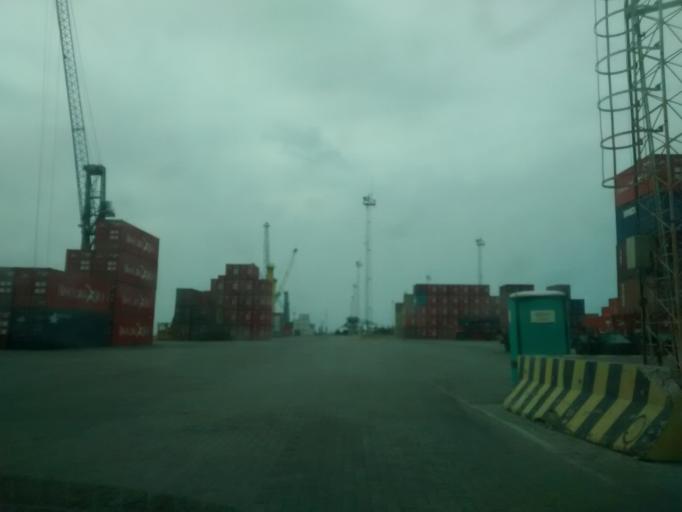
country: BR
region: Ceara
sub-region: Caucaia
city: Cambebba
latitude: -3.5306
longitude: -38.7933
